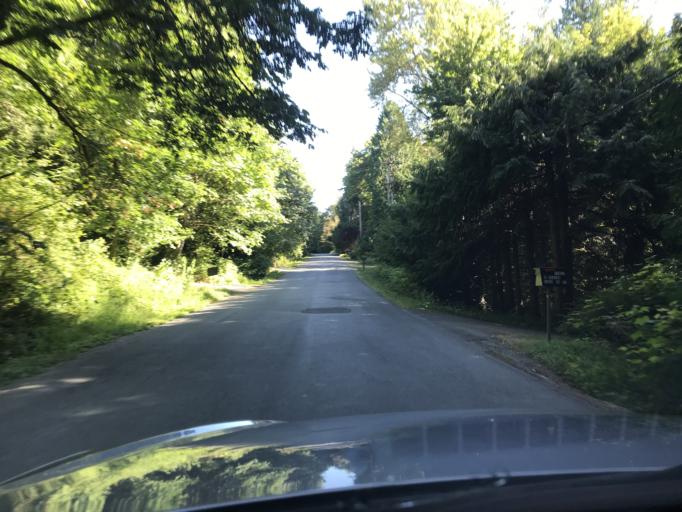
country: US
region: Washington
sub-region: King County
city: Maple Heights-Lake Desire
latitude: 47.4413
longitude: -122.0826
